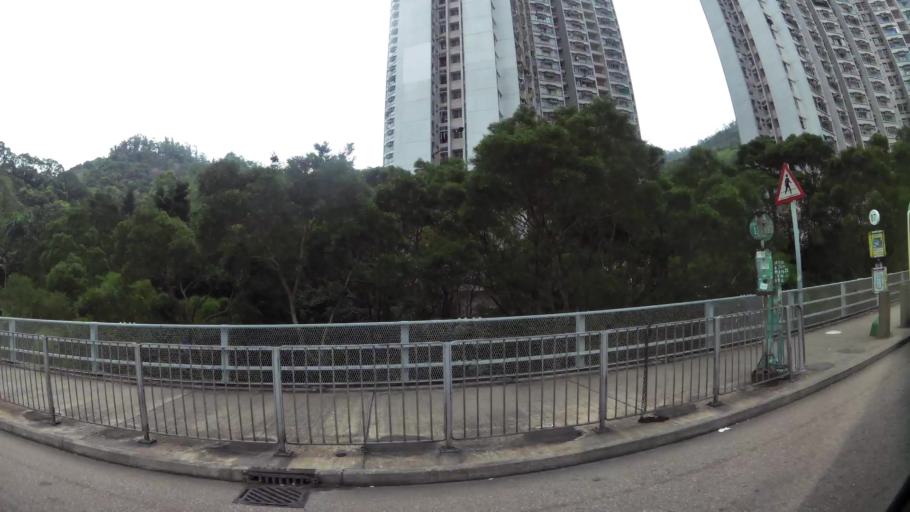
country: HK
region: Kowloon City
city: Kowloon
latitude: 22.3095
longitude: 114.2388
